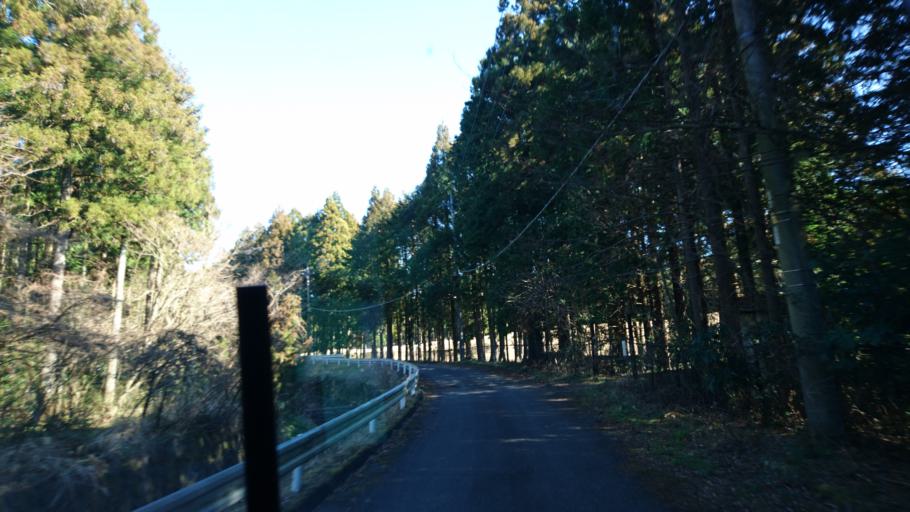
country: JP
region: Shizuoka
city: Fujinomiya
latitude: 35.3272
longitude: 138.5812
